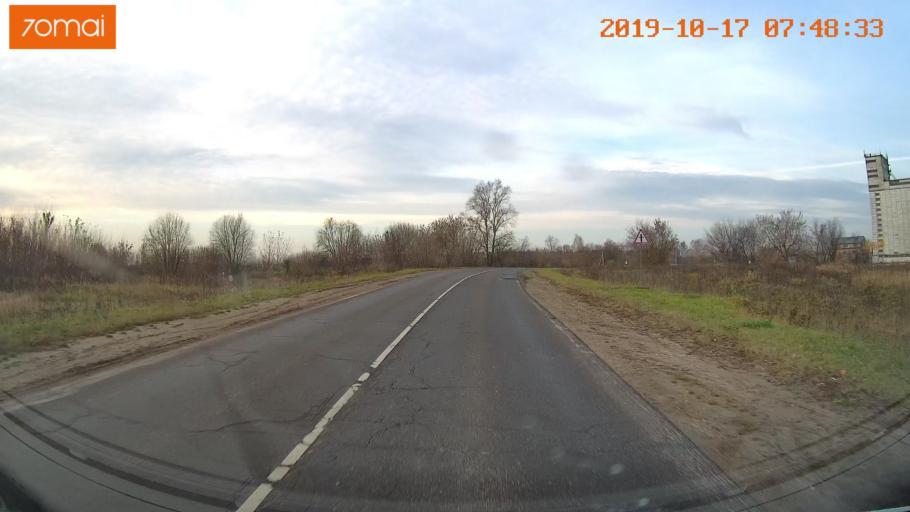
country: RU
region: Vladimir
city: Yur'yev-Pol'skiy
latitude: 56.4789
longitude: 39.6747
